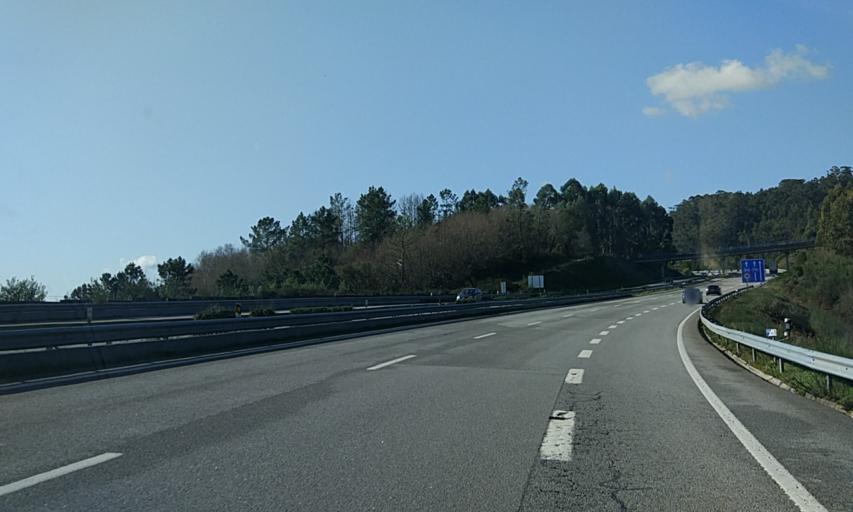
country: PT
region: Aveiro
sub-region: Sever do Vouga
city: Sever do Vouga
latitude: 40.6802
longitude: -8.2730
